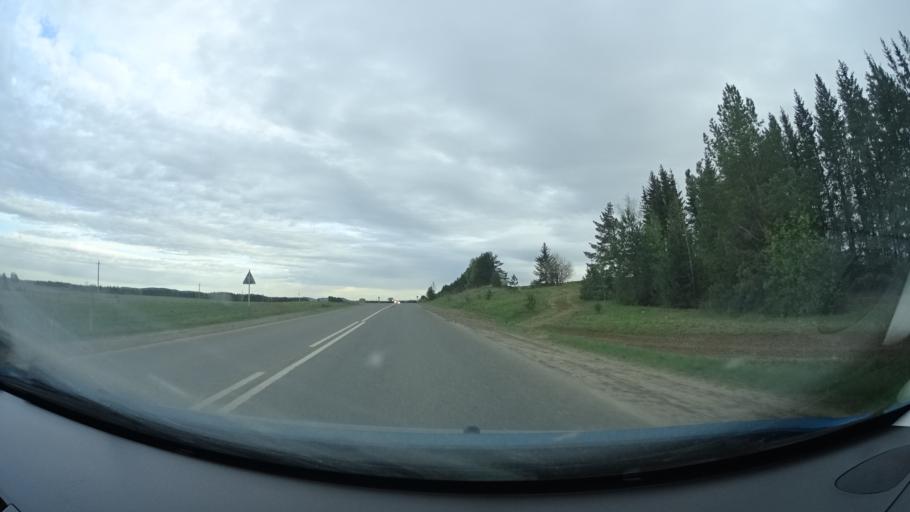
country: RU
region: Perm
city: Osa
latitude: 57.2691
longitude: 55.5718
